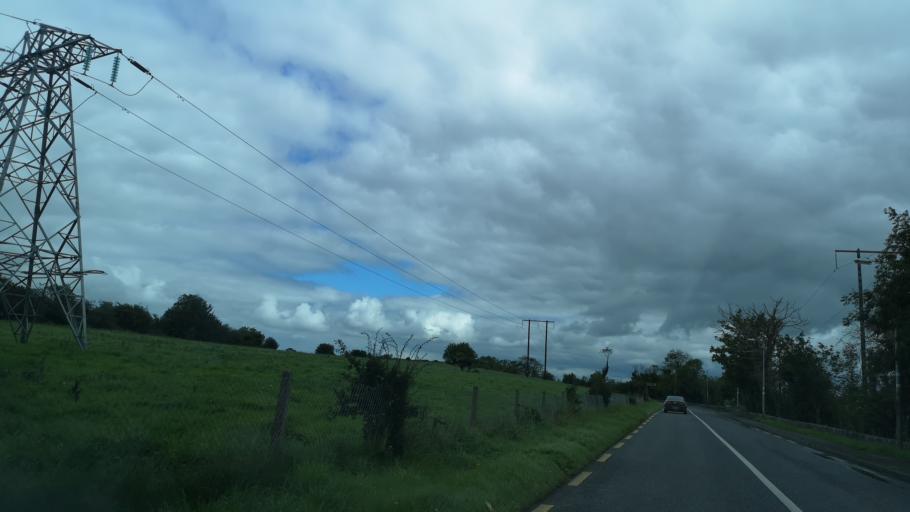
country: IE
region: Leinster
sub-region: Uibh Fhaili
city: Banagher
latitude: 53.2785
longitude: -8.0599
